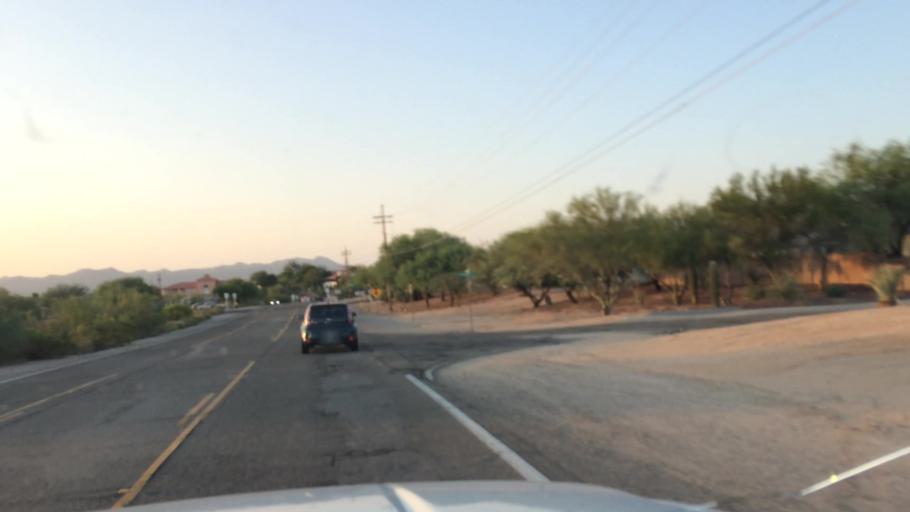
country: US
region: Arizona
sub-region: Pima County
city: Casas Adobes
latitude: 32.3448
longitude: -111.0204
